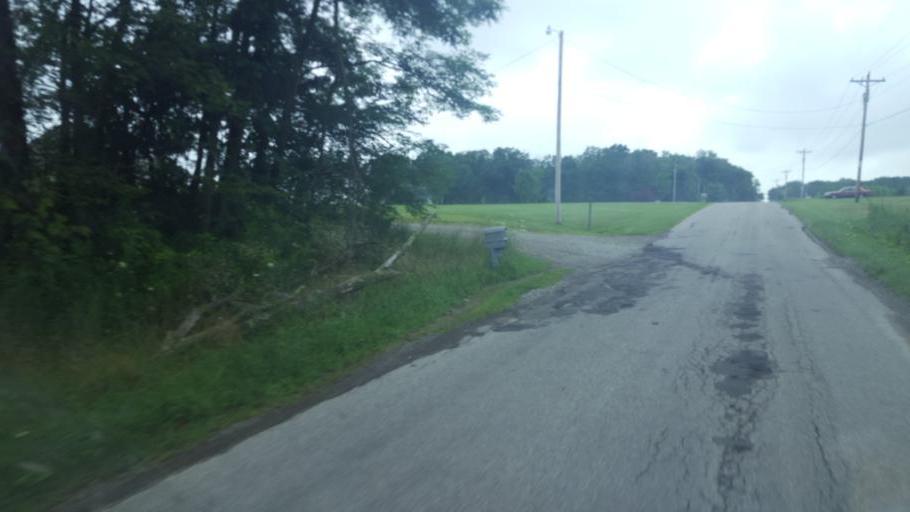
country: US
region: Ohio
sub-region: Morrow County
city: Cardington
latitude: 40.4145
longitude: -82.7875
